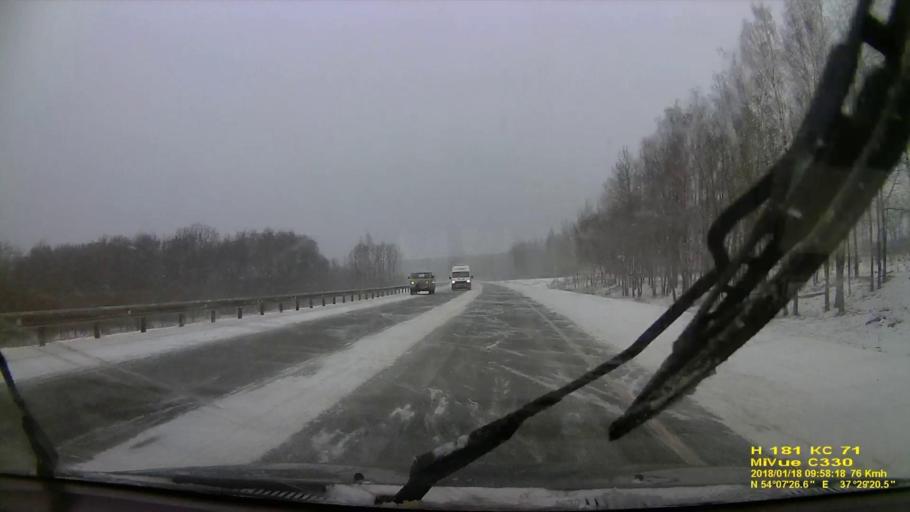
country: RU
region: Tula
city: Kosaya Gora
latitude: 54.1239
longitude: 37.4890
